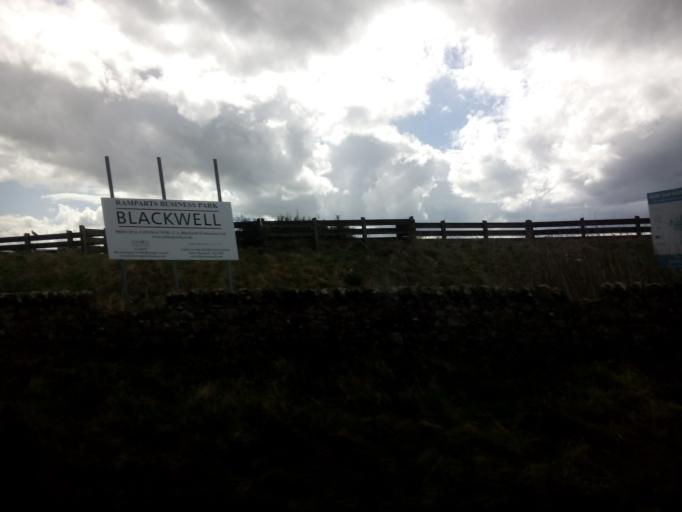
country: GB
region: England
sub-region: Northumberland
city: Berwick-Upon-Tweed
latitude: 55.7923
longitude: -2.0157
